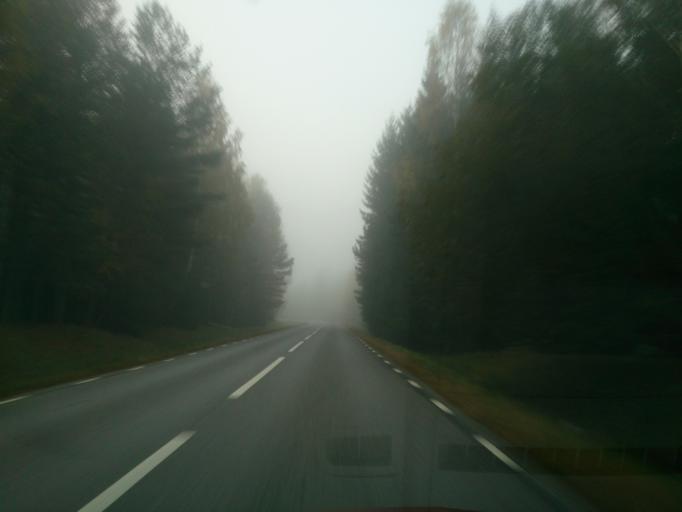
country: SE
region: OEstergoetland
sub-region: Atvidabergs Kommun
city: Atvidaberg
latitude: 58.1255
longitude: 15.9516
